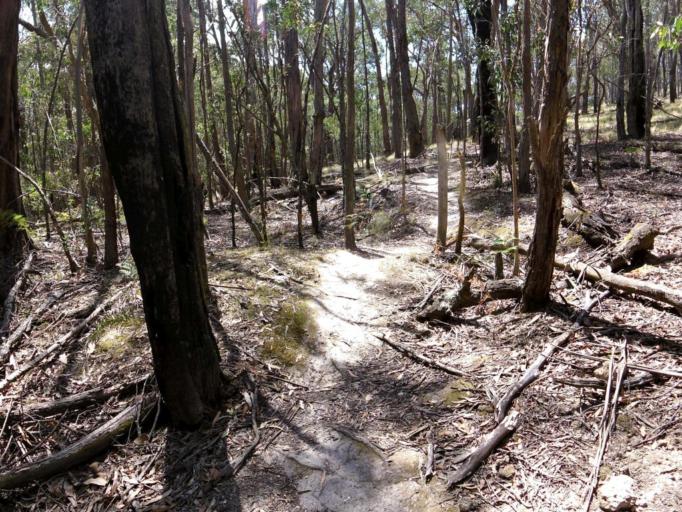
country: AU
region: Victoria
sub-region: Melton
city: Melton West
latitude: -37.4907
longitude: 144.5382
